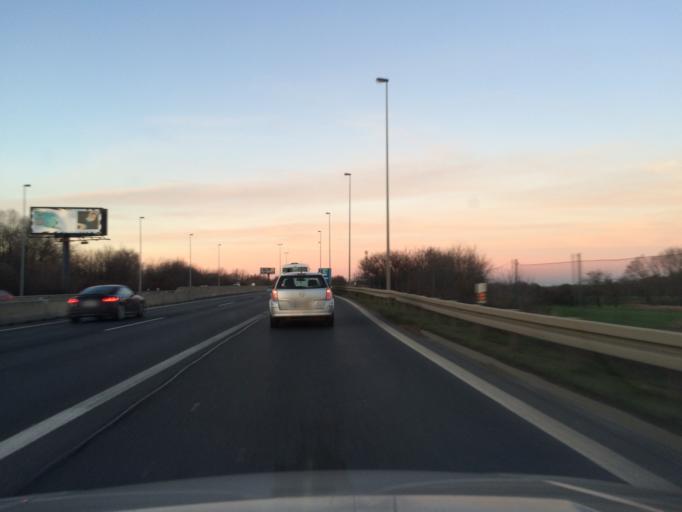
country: CZ
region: Central Bohemia
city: Hostivice
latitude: 50.0960
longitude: 14.2962
